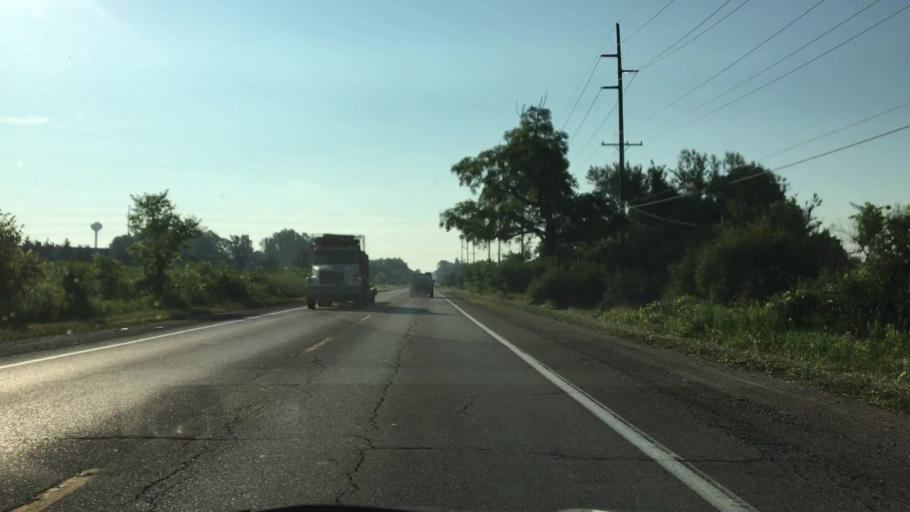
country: US
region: Michigan
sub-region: Oakland County
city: Wixom
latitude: 42.5061
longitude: -83.5901
